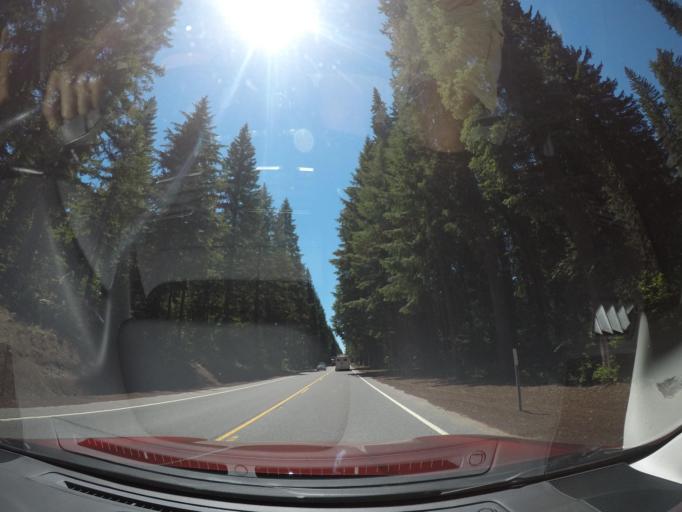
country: US
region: Oregon
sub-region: Deschutes County
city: Sisters
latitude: 44.5378
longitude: -121.9950
